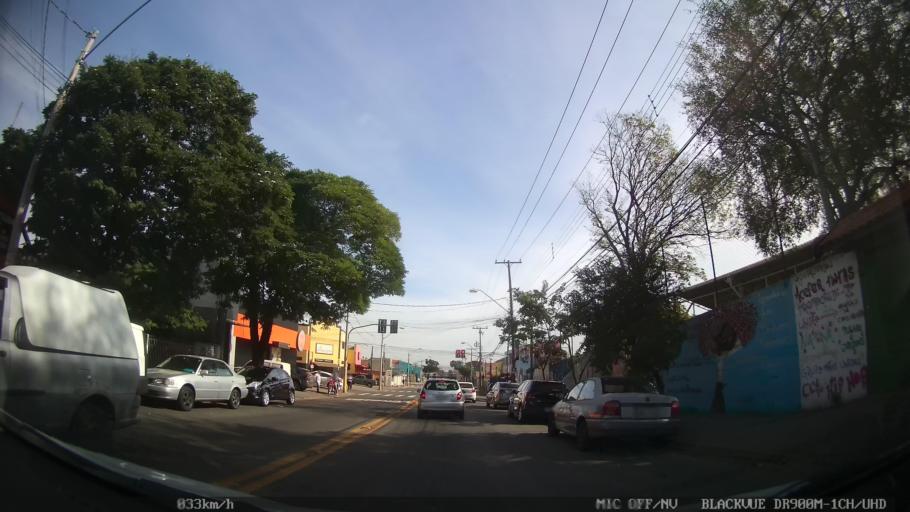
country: BR
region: Sao Paulo
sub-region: Piracicaba
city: Piracicaba
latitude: -22.7518
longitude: -47.6510
